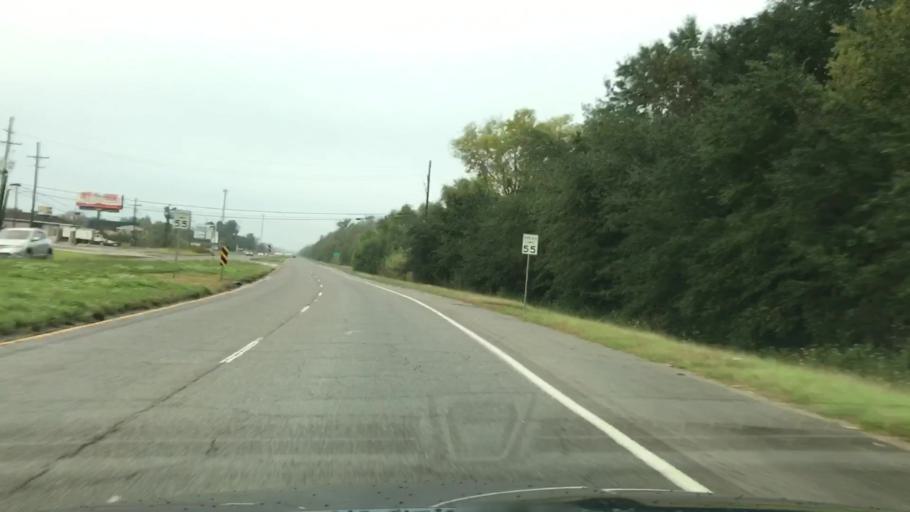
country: US
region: Louisiana
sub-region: Saint Charles Parish
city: Des Allemands
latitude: 29.8205
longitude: -90.4838
